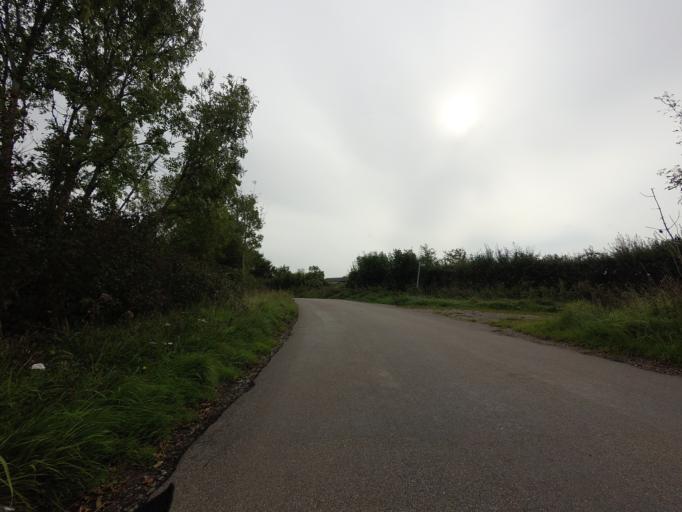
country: GB
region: England
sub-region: Hertfordshire
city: Reed
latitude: 51.9873
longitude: 0.0311
